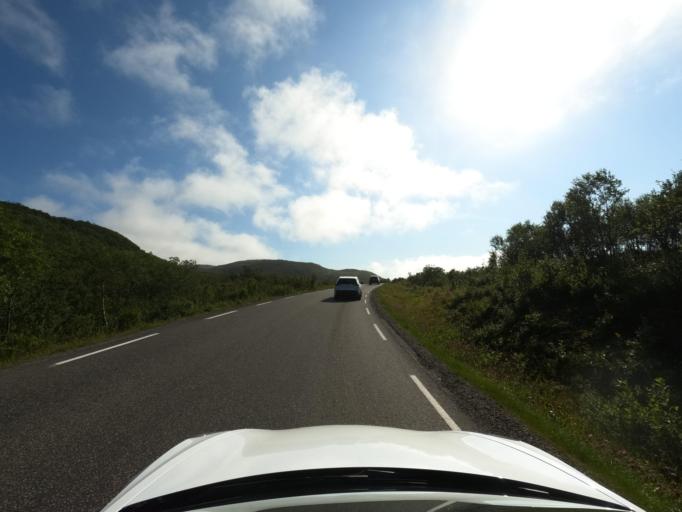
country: NO
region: Nordland
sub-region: Vestvagoy
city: Evjen
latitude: 68.2875
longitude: 13.8599
